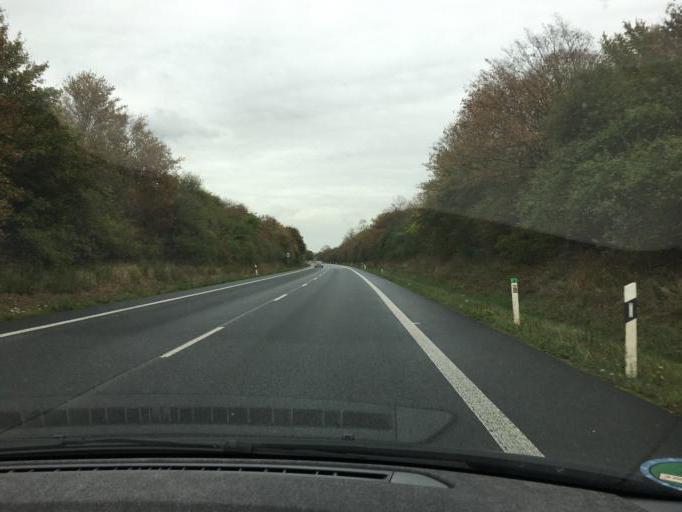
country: DE
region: North Rhine-Westphalia
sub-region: Regierungsbezirk Koln
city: Niederzier
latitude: 50.9475
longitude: 6.4933
